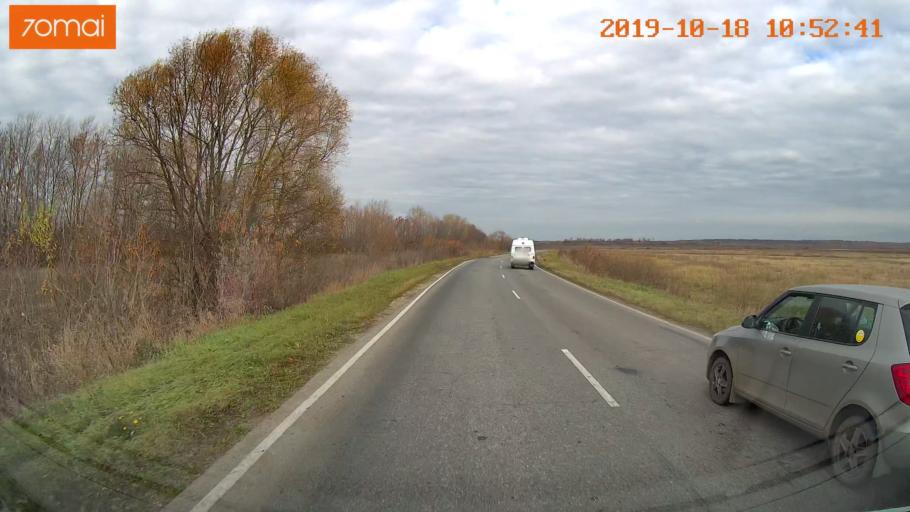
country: RU
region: Tula
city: Yepifan'
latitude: 53.7696
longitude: 38.6482
